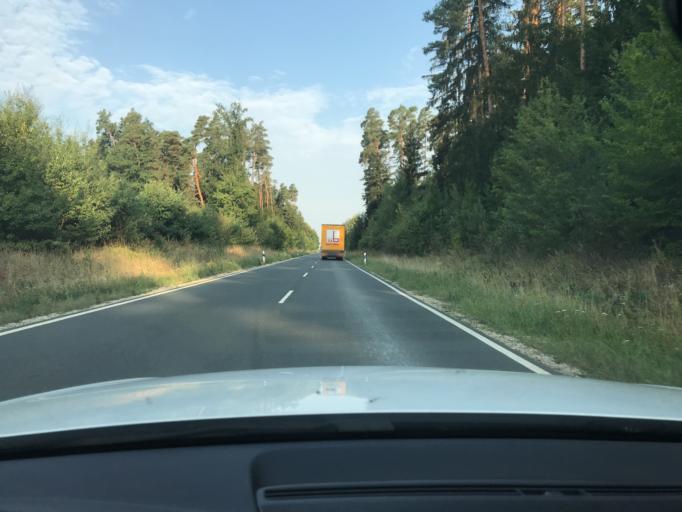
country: DE
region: Bavaria
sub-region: Regierungsbezirk Mittelfranken
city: Simmelsdorf
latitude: 49.5743
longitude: 11.2931
